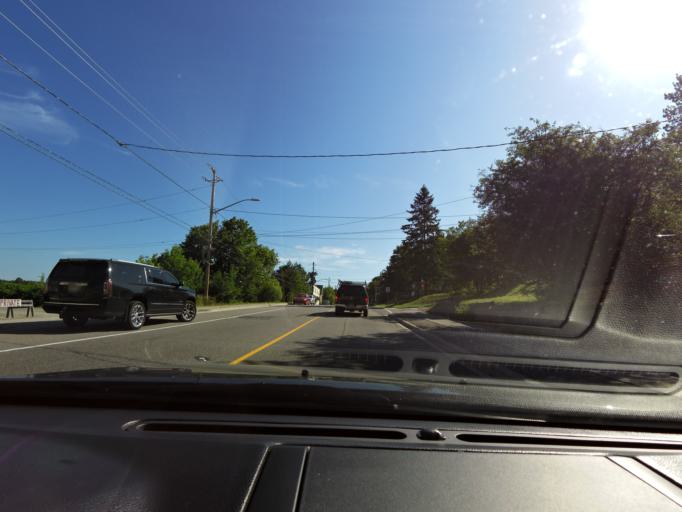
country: CA
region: Ontario
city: Huntsville
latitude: 45.3239
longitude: -79.2244
